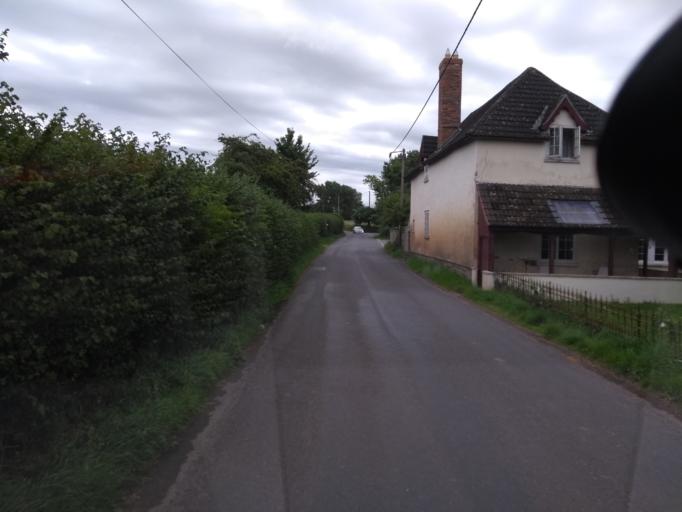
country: GB
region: England
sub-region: Somerset
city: Bishops Lydeard
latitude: 51.1826
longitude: -3.1536
